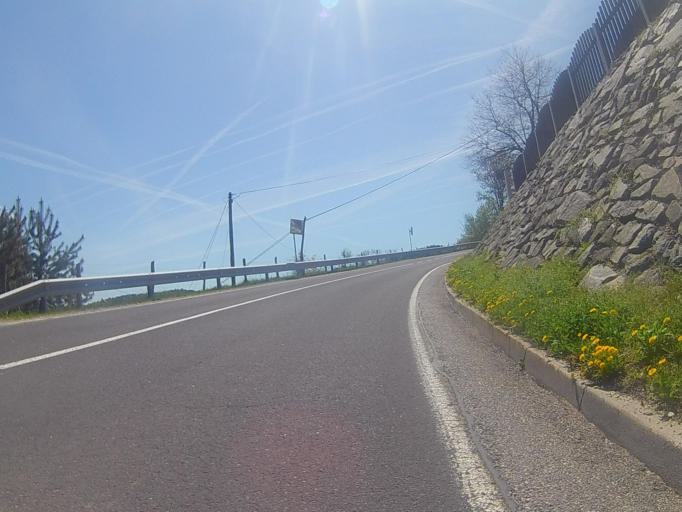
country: SI
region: Race-Fram
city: Fram
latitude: 46.4880
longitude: 15.6031
